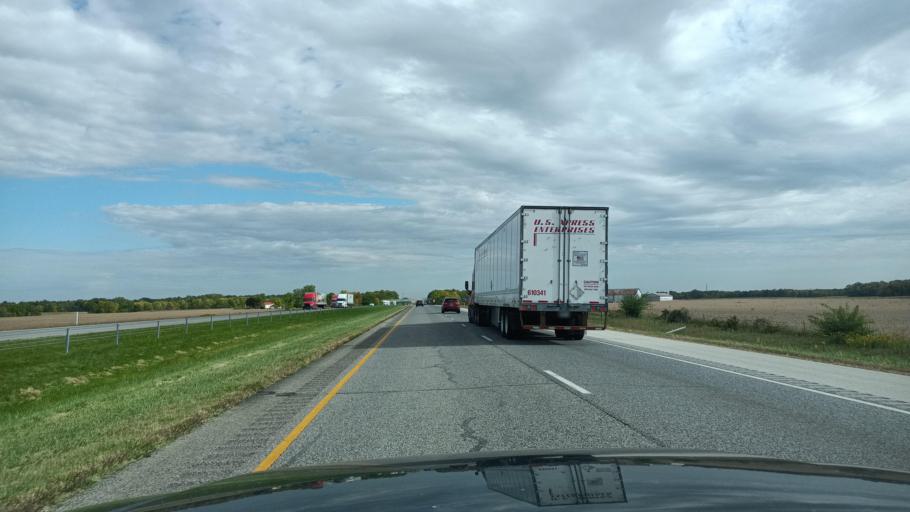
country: US
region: Indiana
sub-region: Huntington County
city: Warren
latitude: 40.6919
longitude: -85.4724
